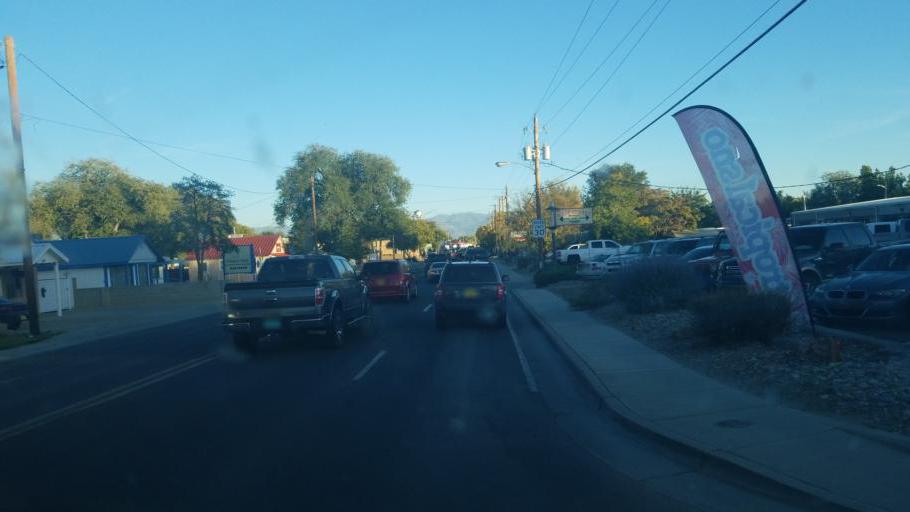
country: US
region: New Mexico
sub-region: Valencia County
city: Los Lunas
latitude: 34.8097
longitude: -106.7398
